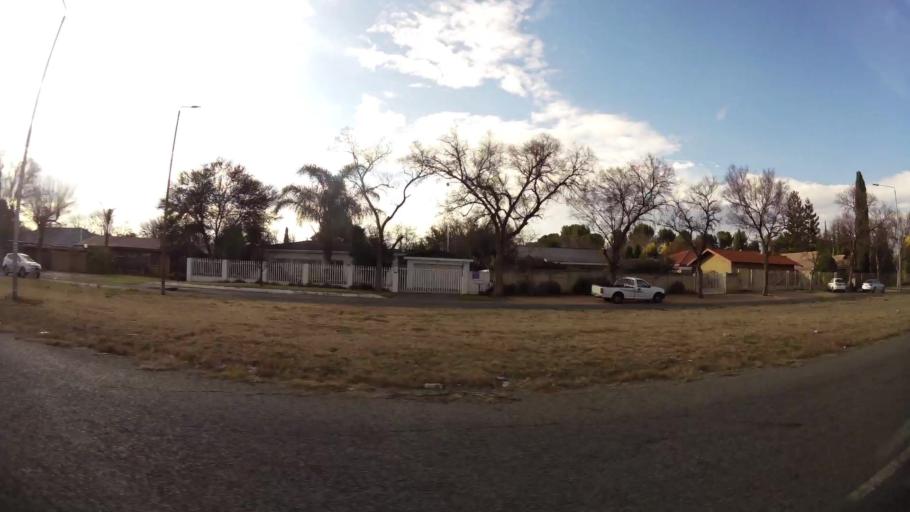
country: ZA
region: Orange Free State
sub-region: Lejweleputswa District Municipality
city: Welkom
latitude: -27.9867
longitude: 26.7218
